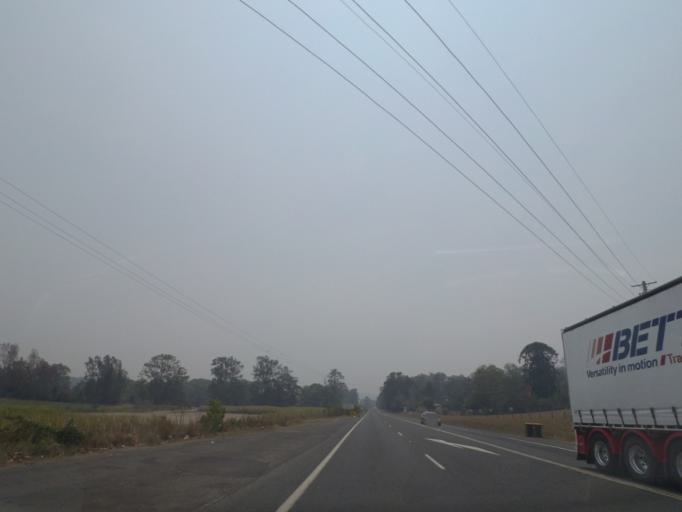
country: AU
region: New South Wales
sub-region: Clarence Valley
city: Maclean
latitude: -29.5609
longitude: 153.1490
